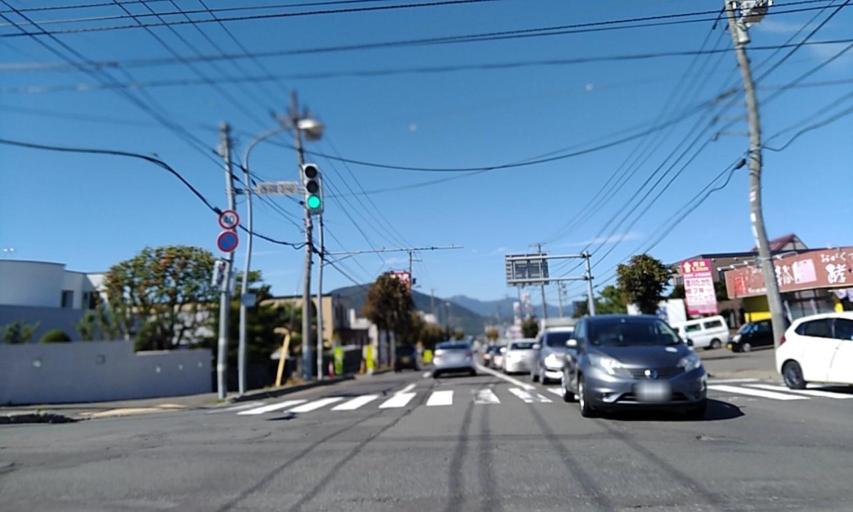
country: JP
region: Hokkaido
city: Sapporo
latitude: 43.0058
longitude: 141.3854
